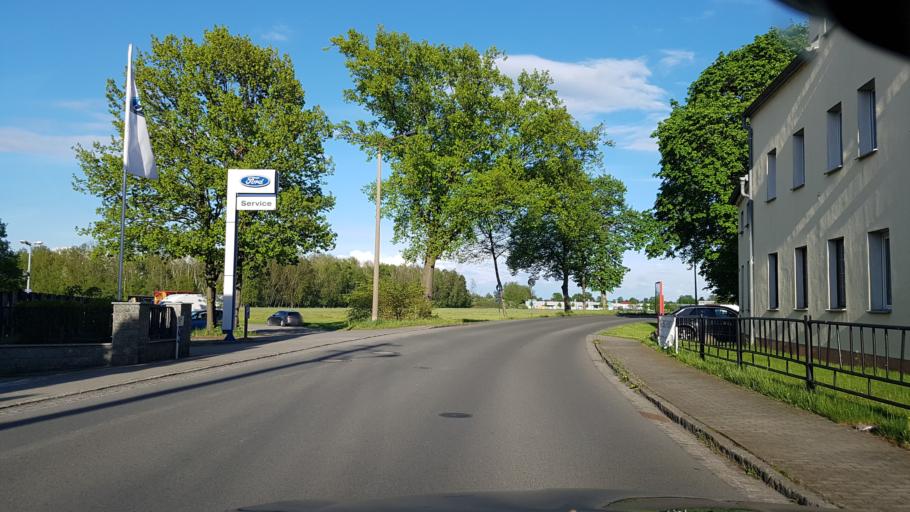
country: DE
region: Brandenburg
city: Lauchhammer
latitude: 51.4720
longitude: 13.7508
